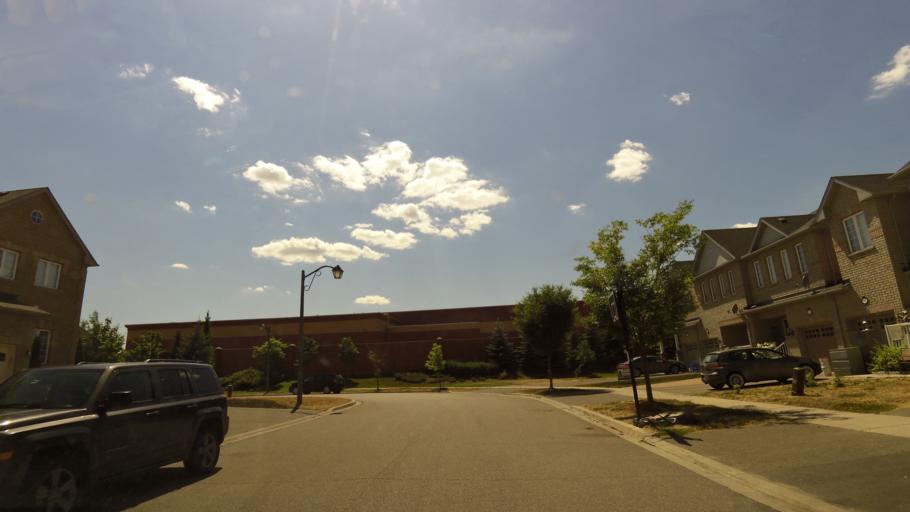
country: CA
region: Ontario
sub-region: Halton
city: Milton
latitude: 43.6332
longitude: -79.8765
